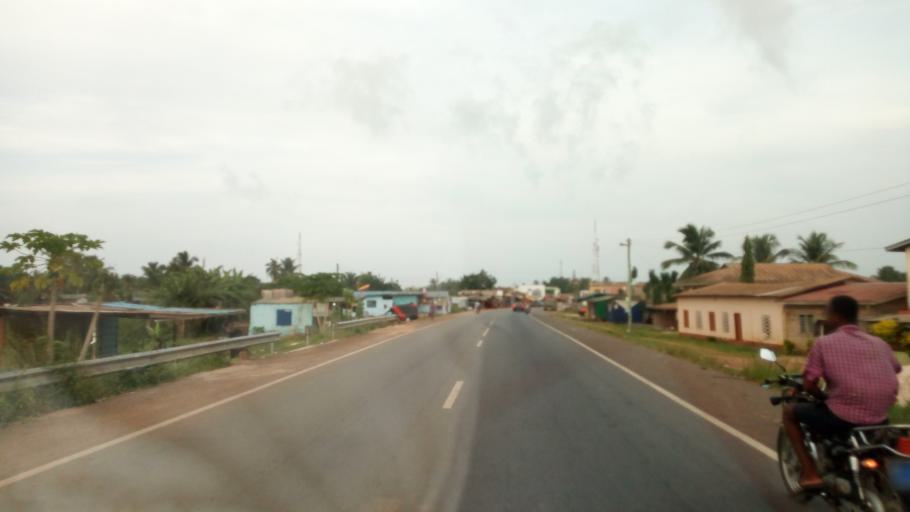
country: GH
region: Volta
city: Keta
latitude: 6.0754
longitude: 1.0401
